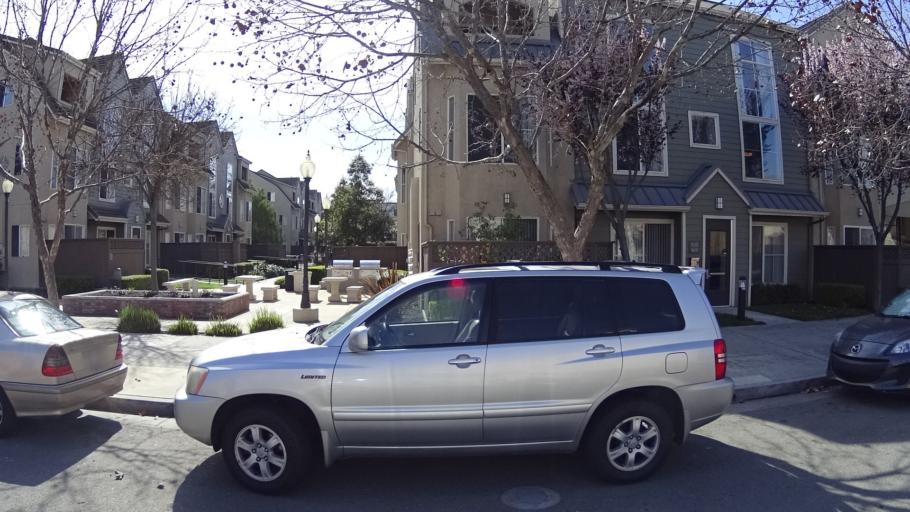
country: US
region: California
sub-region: Santa Clara County
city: San Jose
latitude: 37.3527
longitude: -121.8914
